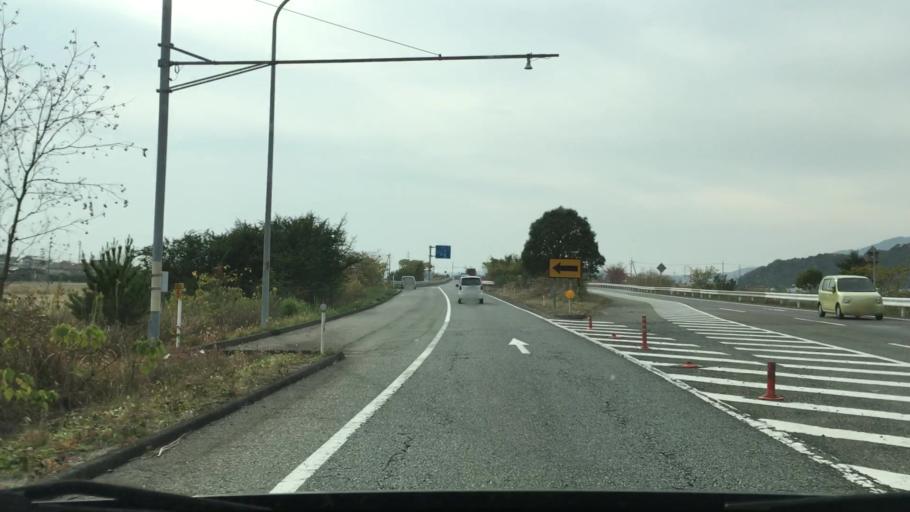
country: JP
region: Yamaguchi
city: Hofu
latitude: 34.0507
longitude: 131.5189
